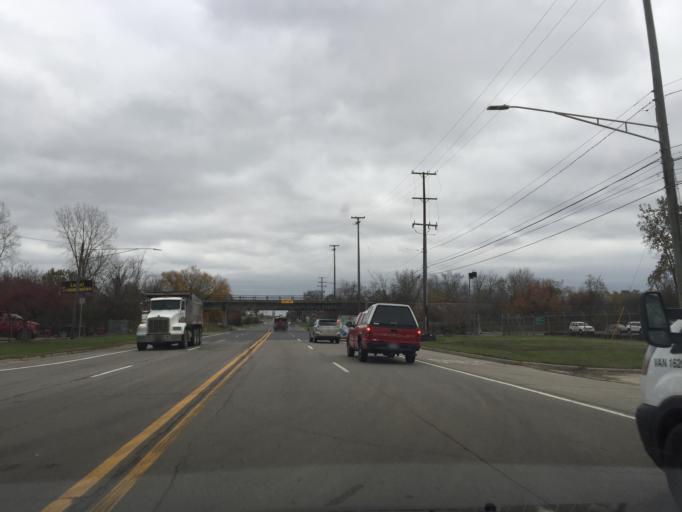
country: US
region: Michigan
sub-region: Oakland County
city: Pontiac
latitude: 42.6623
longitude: -83.3242
